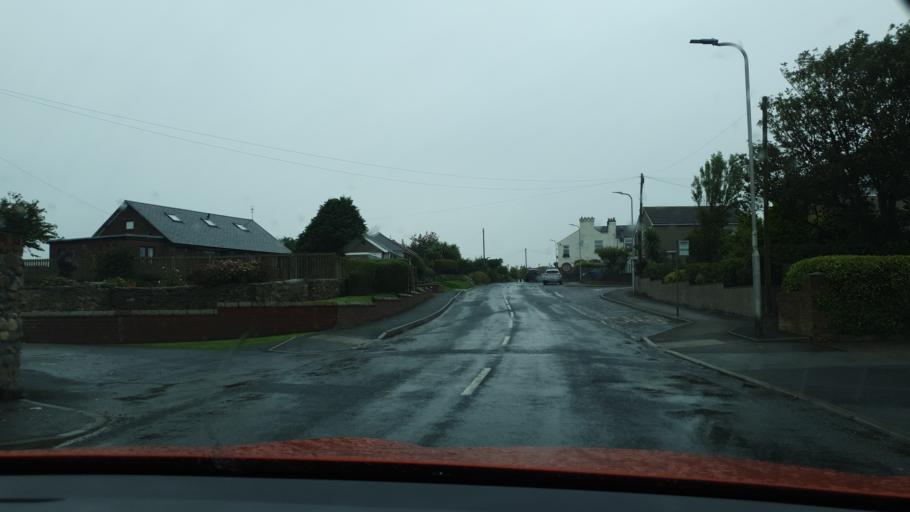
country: GB
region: England
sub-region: Cumbria
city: Barrow in Furness
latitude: 54.1181
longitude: -3.2522
